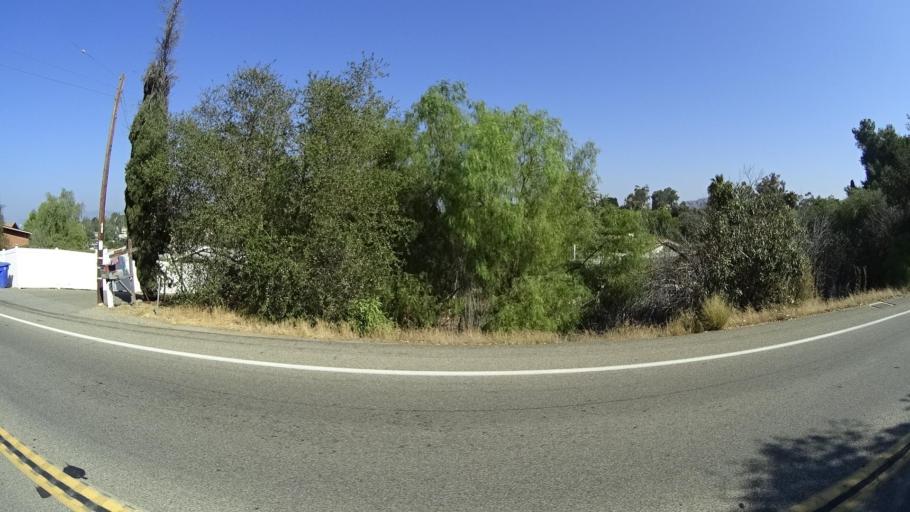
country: US
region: California
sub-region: San Diego County
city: Fallbrook
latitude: 33.3891
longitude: -117.2268
